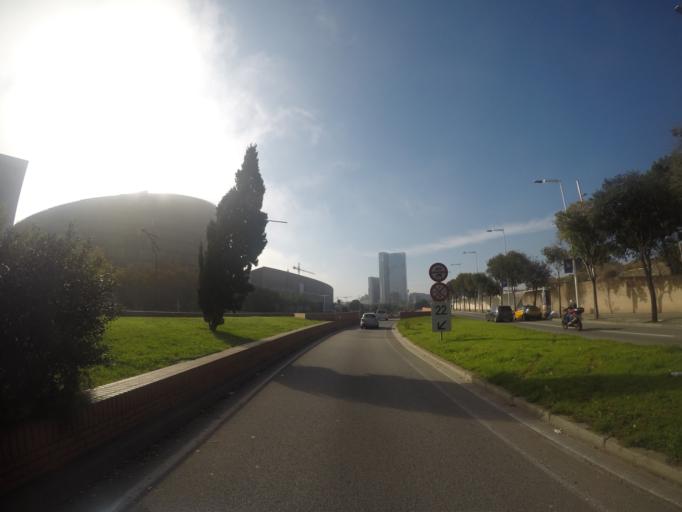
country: ES
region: Catalonia
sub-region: Provincia de Barcelona
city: Ciutat Vella
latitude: 41.3866
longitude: 2.1941
